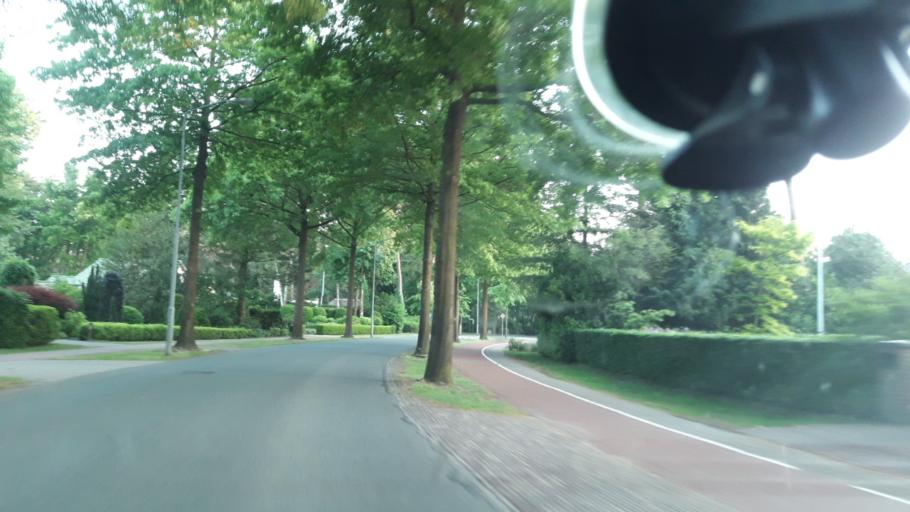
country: NL
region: Gelderland
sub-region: Gemeente Nunspeet
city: Nunspeet
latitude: 52.3751
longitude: 5.7945
